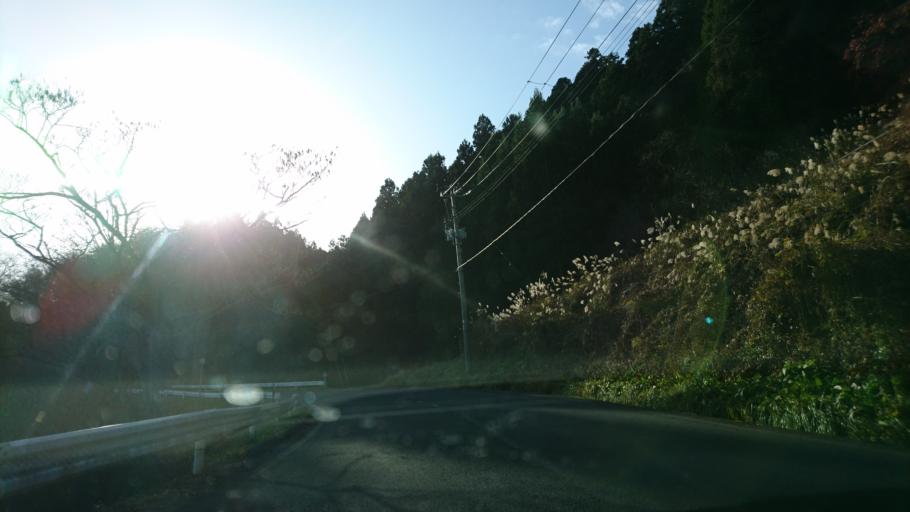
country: JP
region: Iwate
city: Ichinoseki
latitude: 38.8942
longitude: 141.2800
